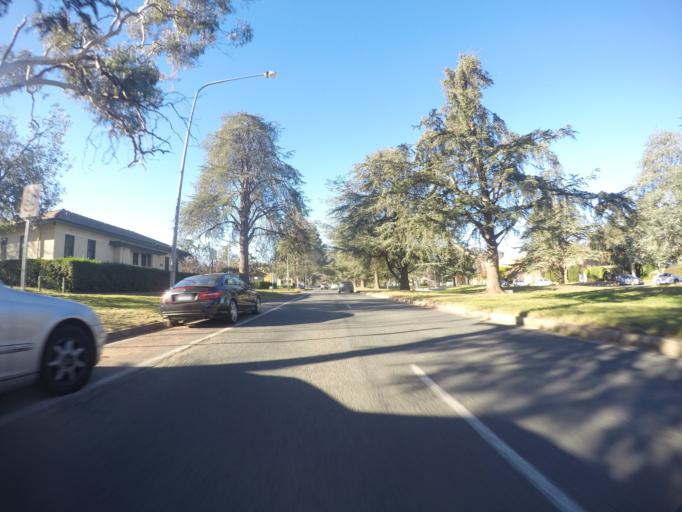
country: AU
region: Australian Capital Territory
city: Canberra
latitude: -35.2784
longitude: 149.1374
